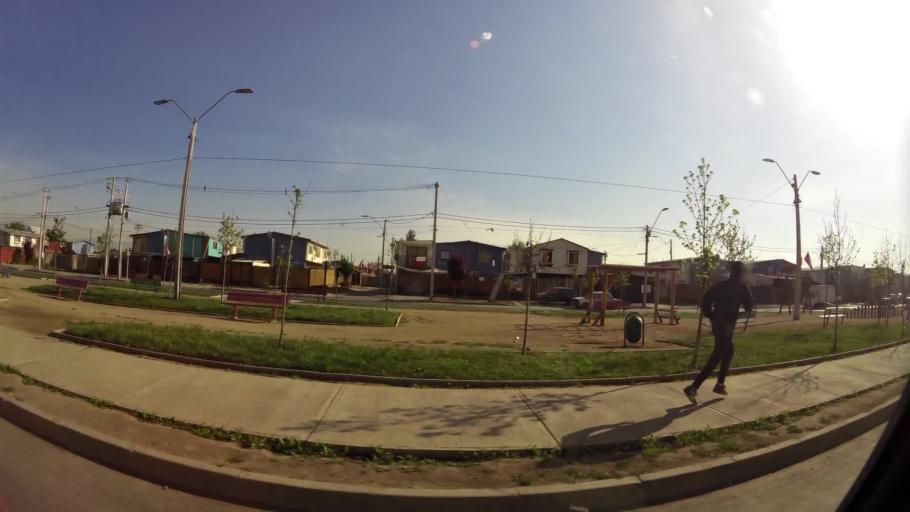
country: CL
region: Santiago Metropolitan
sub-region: Provincia de Santiago
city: Lo Prado
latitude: -33.4198
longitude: -70.7646
